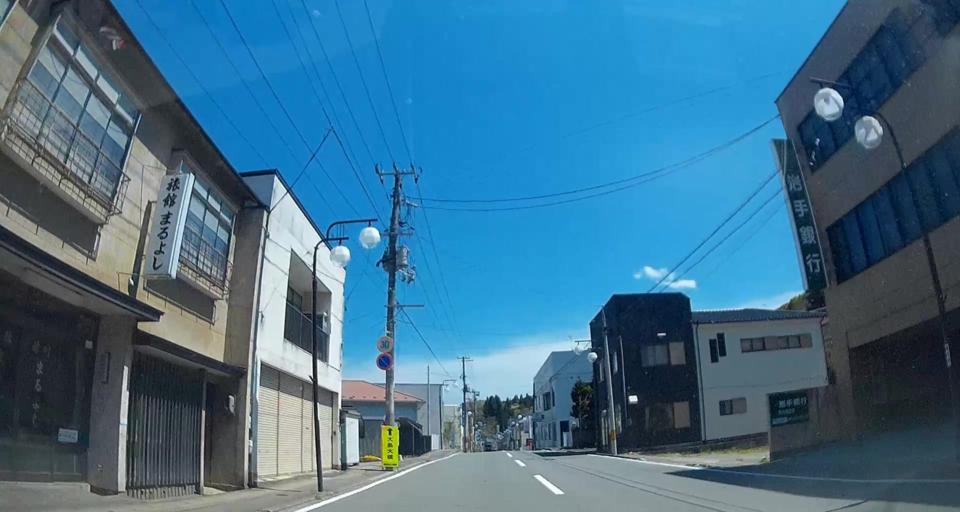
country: JP
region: Iwate
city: Ofunato
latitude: 38.9079
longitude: 141.5611
